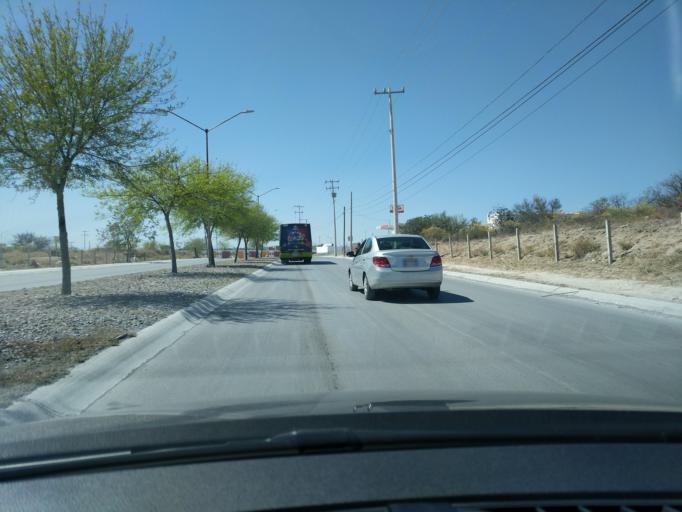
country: MX
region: Nuevo Leon
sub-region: Juarez
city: San Antonio
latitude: 25.6484
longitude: -100.0671
